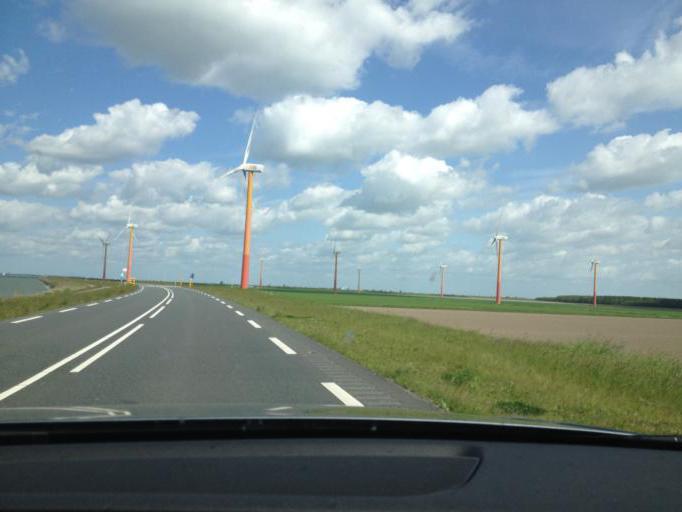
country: NL
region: North Holland
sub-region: Gemeente Naarden
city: Naarden
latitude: 52.3654
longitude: 5.1316
